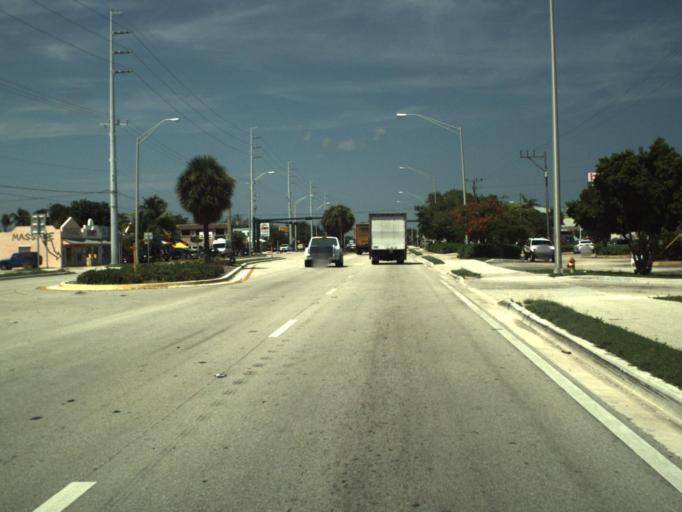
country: US
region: Florida
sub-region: Monroe County
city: Marathon
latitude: 24.7292
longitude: -81.0357
